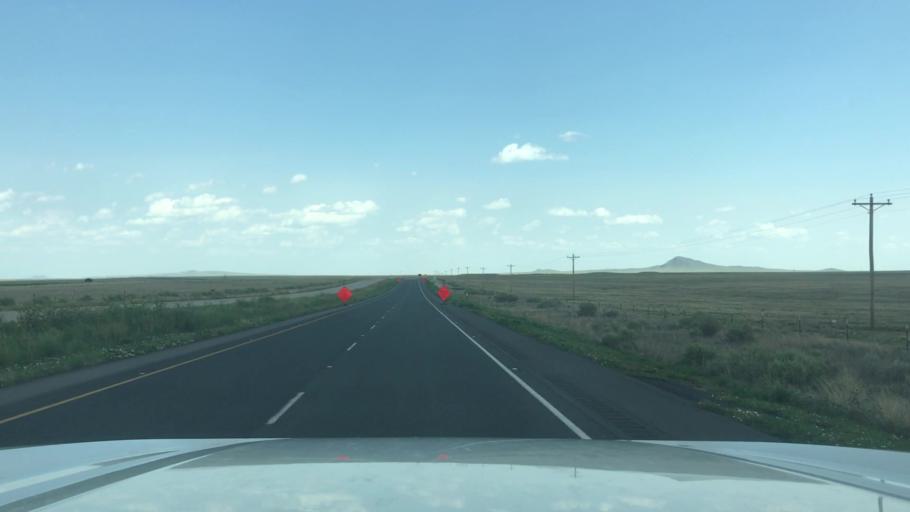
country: US
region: New Mexico
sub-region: Union County
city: Clayton
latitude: 36.6203
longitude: -103.6951
